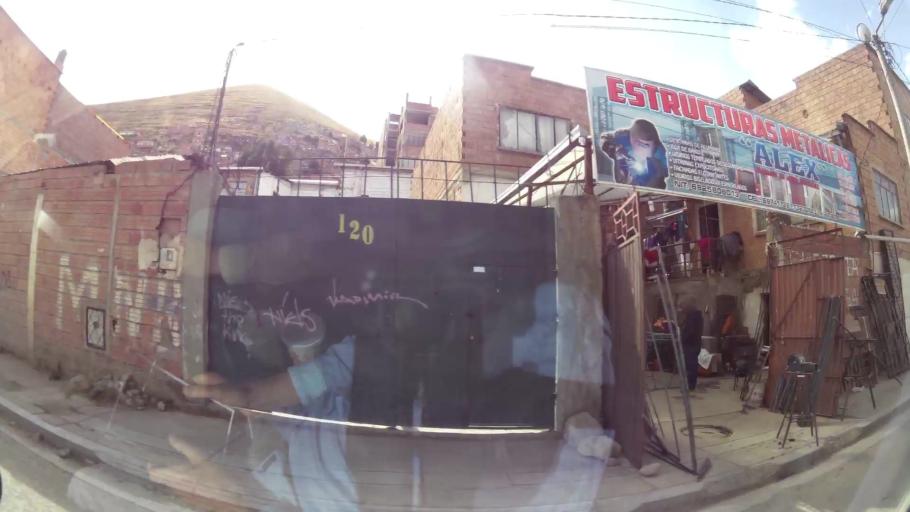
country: BO
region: La Paz
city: La Paz
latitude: -16.4600
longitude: -68.1046
